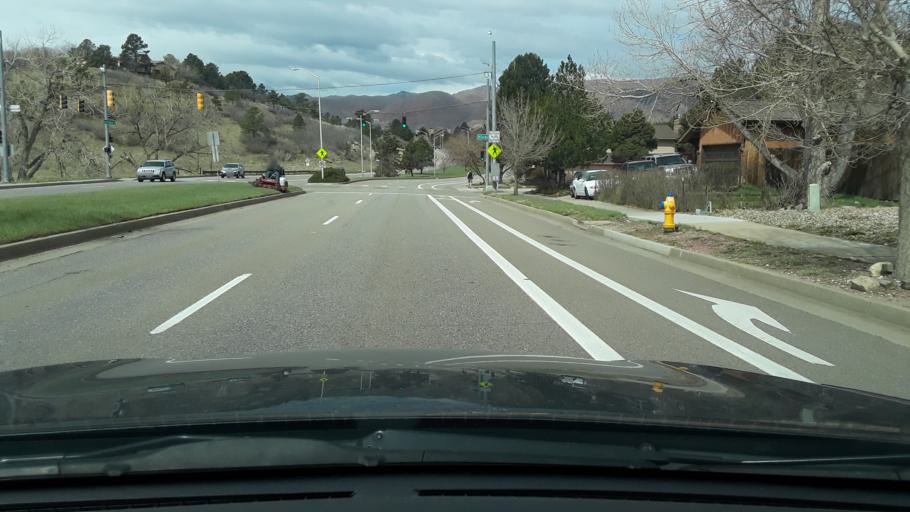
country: US
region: Colorado
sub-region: El Paso County
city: Air Force Academy
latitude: 38.9294
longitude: -104.8242
